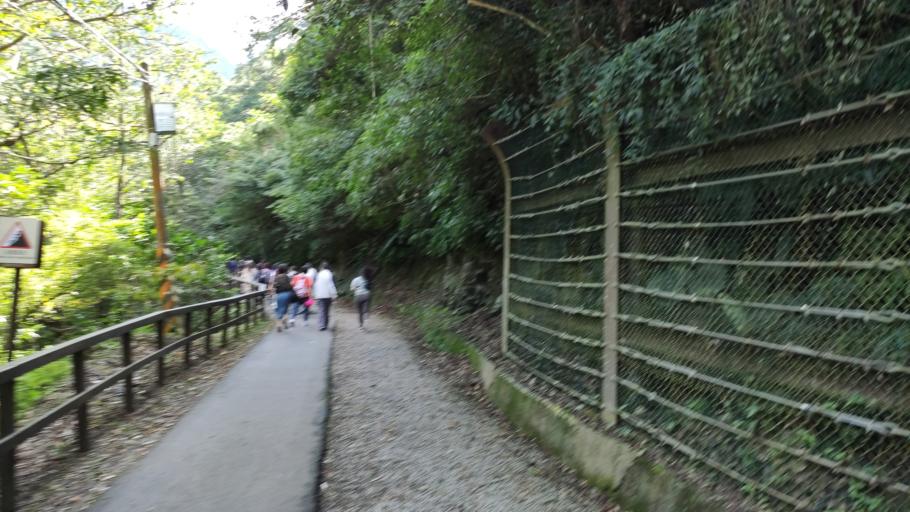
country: TW
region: Taiwan
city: Daxi
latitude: 24.8273
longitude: 121.4470
